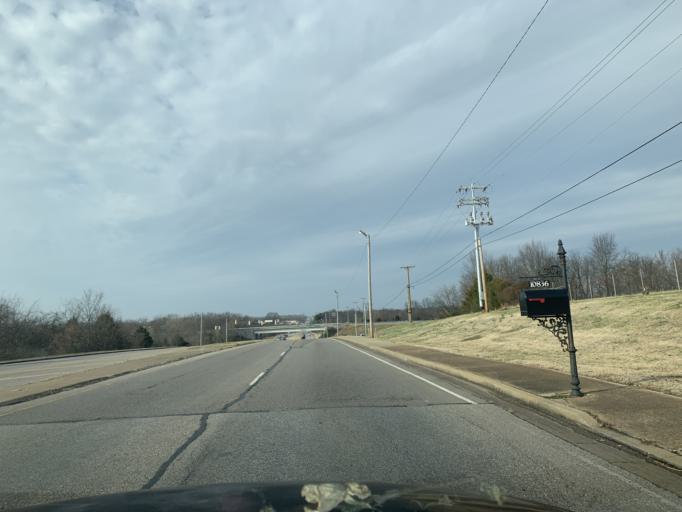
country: US
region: Tennessee
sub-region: Rutherford County
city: Smyrna
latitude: 35.9520
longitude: -86.5123
